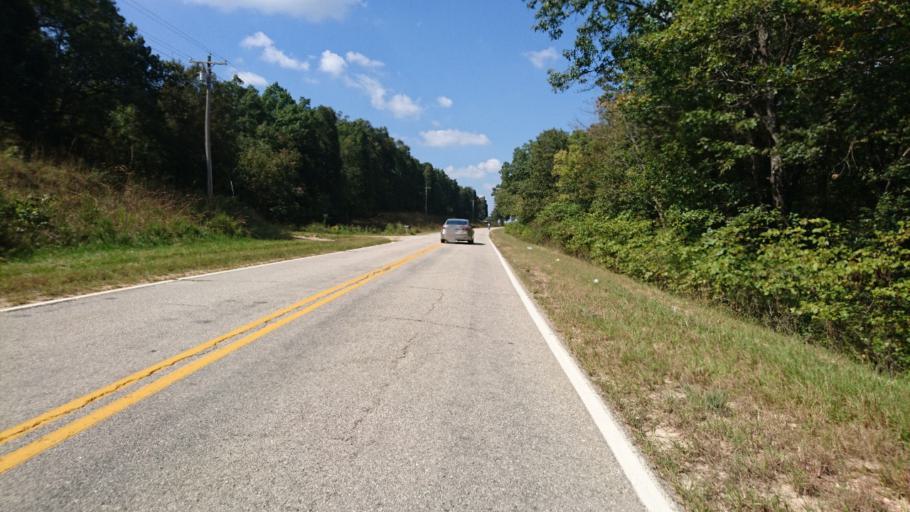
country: US
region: Missouri
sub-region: Pulaski County
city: Richland
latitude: 37.7524
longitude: -92.5003
